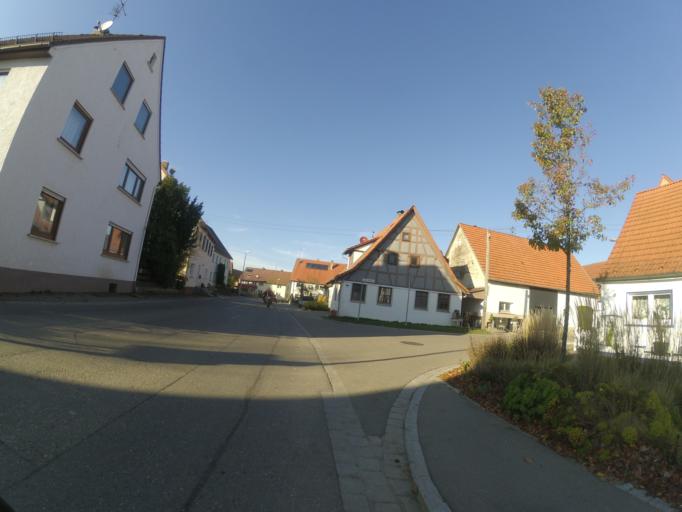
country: DE
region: Baden-Wuerttemberg
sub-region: Tuebingen Region
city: Blaubeuren
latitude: 48.4356
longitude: 9.8186
